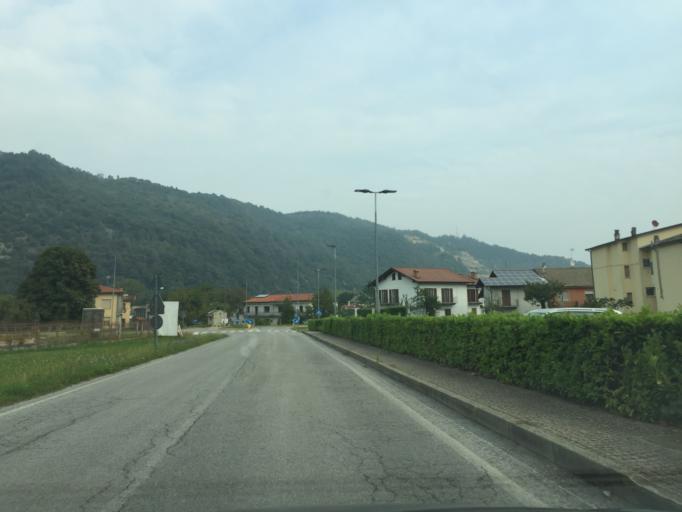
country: IT
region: Piedmont
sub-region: Provincia di Cuneo
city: Roccaforte Mondovi
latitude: 44.3172
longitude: 7.7429
